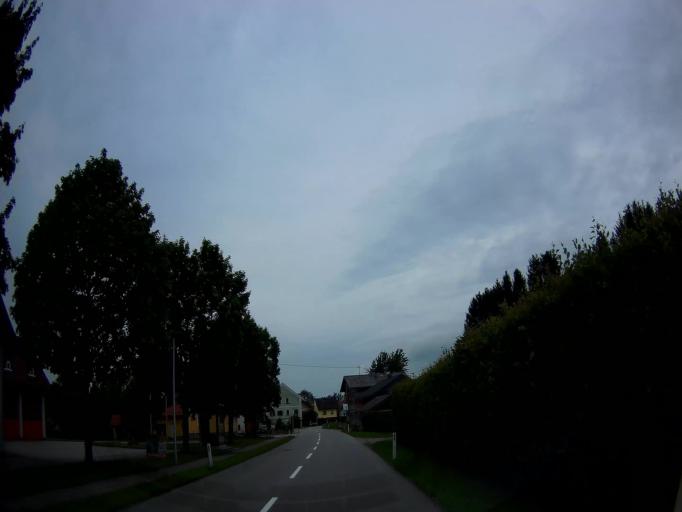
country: AT
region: Salzburg
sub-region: Politischer Bezirk Salzburg-Umgebung
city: Mattsee
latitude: 48.0752
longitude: 13.1425
